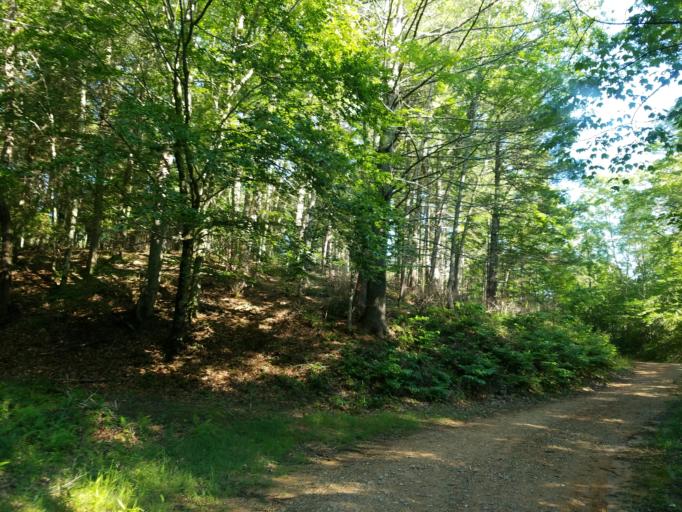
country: US
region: Georgia
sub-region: Fannin County
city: Blue Ridge
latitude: 34.7995
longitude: -84.1935
